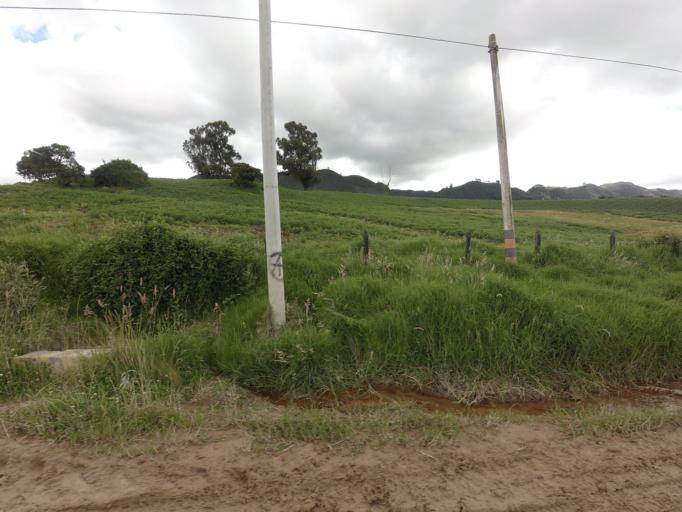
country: CO
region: Cundinamarca
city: Tabio
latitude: 4.9569
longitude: -74.0806
